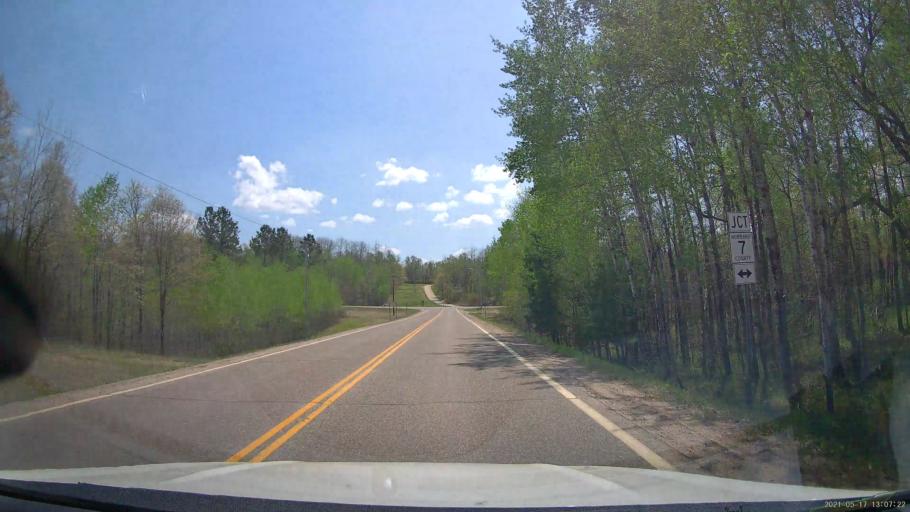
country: US
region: Minnesota
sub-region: Hubbard County
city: Park Rapids
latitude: 47.0474
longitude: -94.9147
